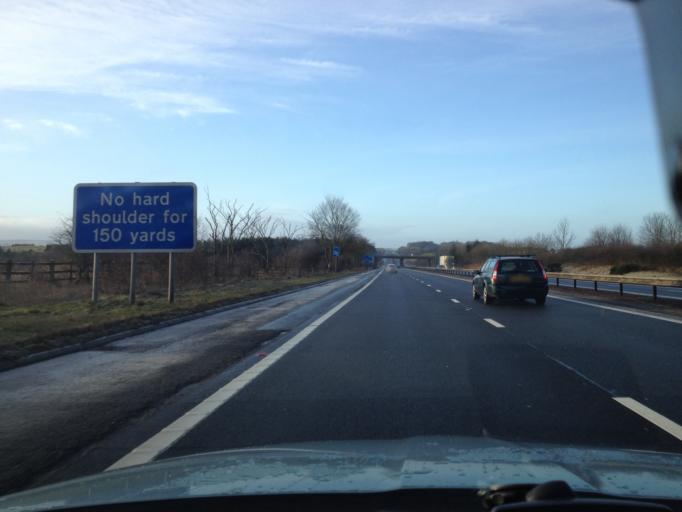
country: GB
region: Scotland
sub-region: West Lothian
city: Blackburn
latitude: 55.8961
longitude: -3.5948
